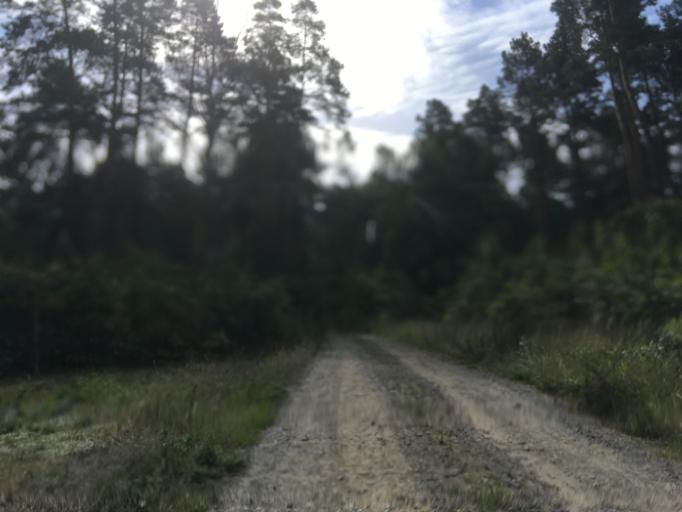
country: DE
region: Brandenburg
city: Birkenwerder
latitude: 52.7526
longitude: 13.3397
